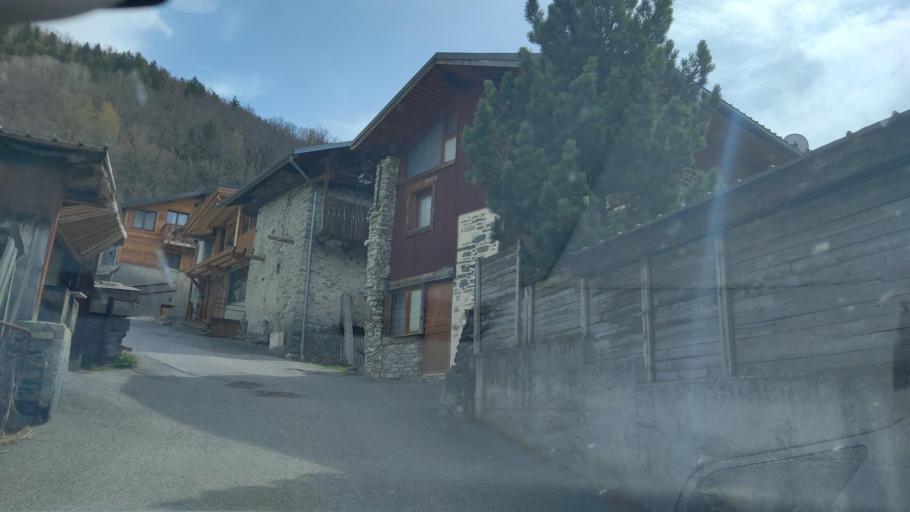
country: FR
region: Rhone-Alpes
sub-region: Departement de la Savoie
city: Bourg-Saint-Maurice
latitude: 45.5854
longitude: 6.7517
